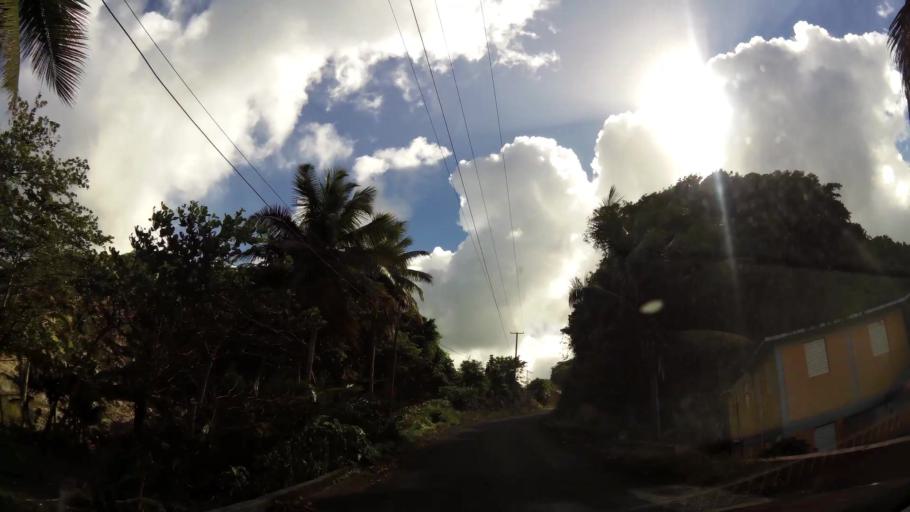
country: DM
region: Saint Andrew
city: Calibishie
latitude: 15.5996
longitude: -61.3948
